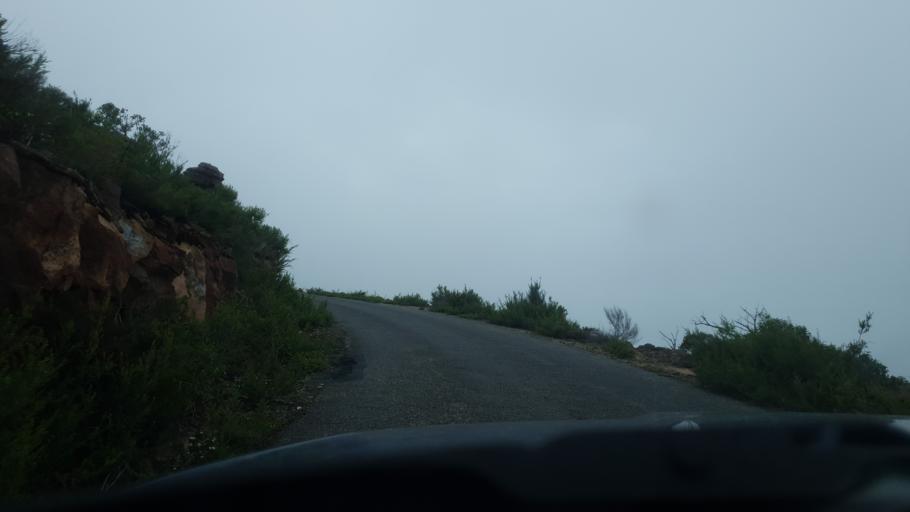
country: AU
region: Victoria
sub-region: Northern Grampians
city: Stawell
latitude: -37.2724
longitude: 142.5810
